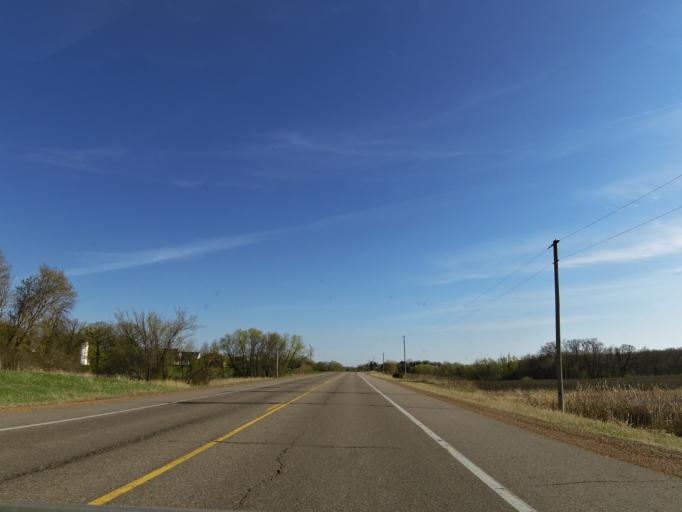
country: US
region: Minnesota
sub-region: Scott County
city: Prior Lake
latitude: 44.7143
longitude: -93.4903
